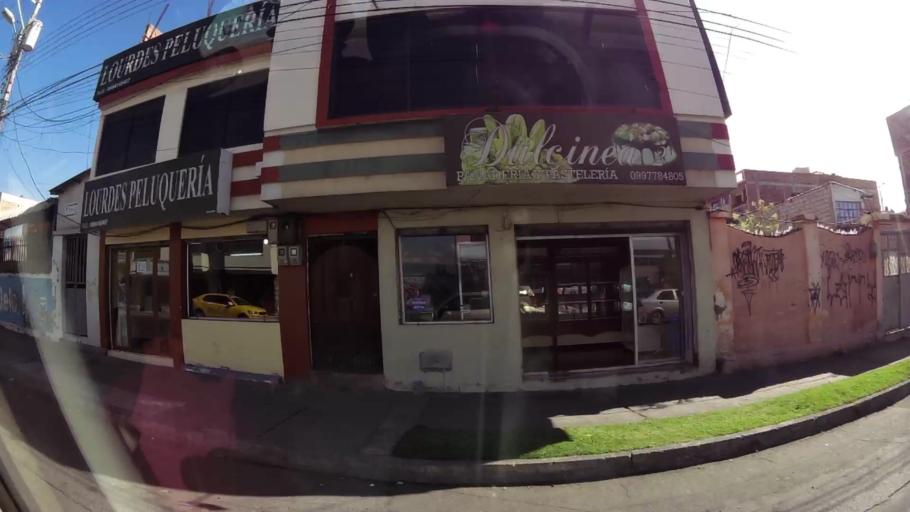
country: EC
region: Chimborazo
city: Riobamba
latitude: -1.6617
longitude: -78.6604
